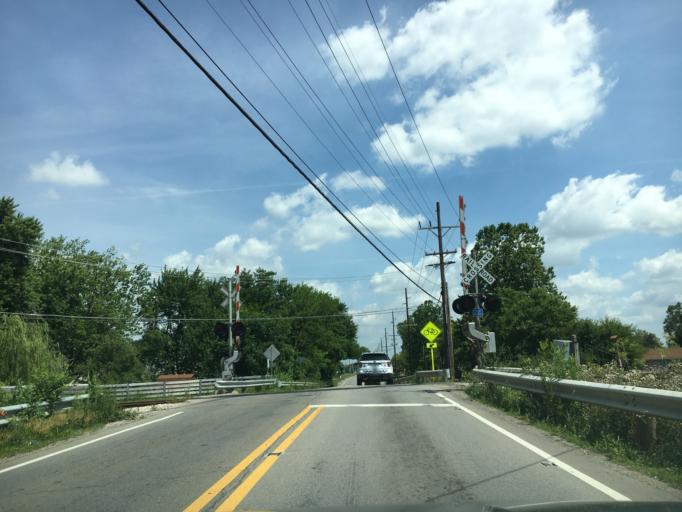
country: US
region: Ohio
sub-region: Franklin County
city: Lincoln Village
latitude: 39.9245
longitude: -83.1441
